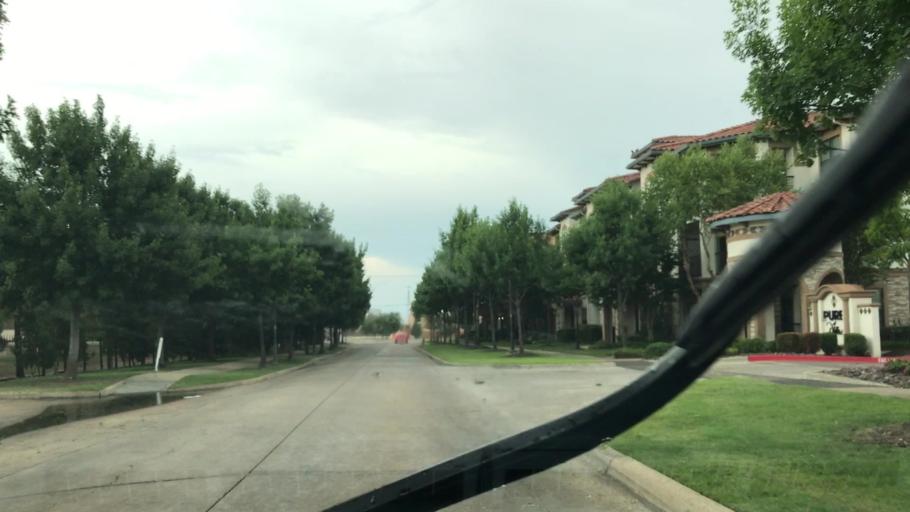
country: US
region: Texas
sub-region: Dallas County
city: Farmers Branch
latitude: 32.8972
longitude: -96.9357
